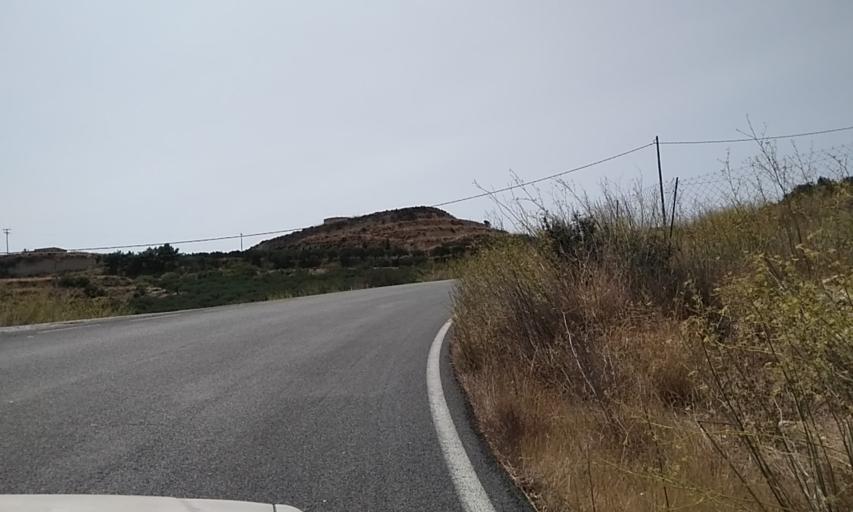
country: GR
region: Crete
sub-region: Nomos Lasithiou
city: Siteia
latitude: 35.1109
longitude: 26.0579
